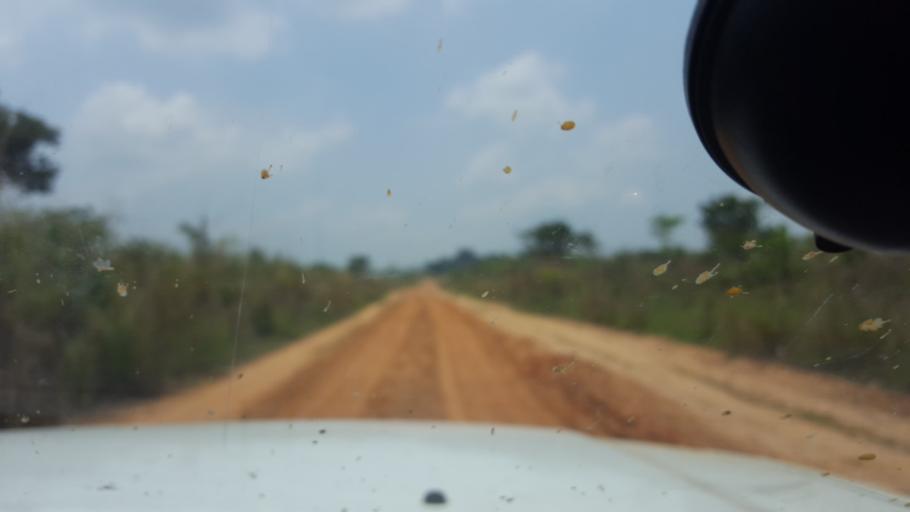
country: CD
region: Bandundu
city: Mushie
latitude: -3.7501
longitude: 16.6627
